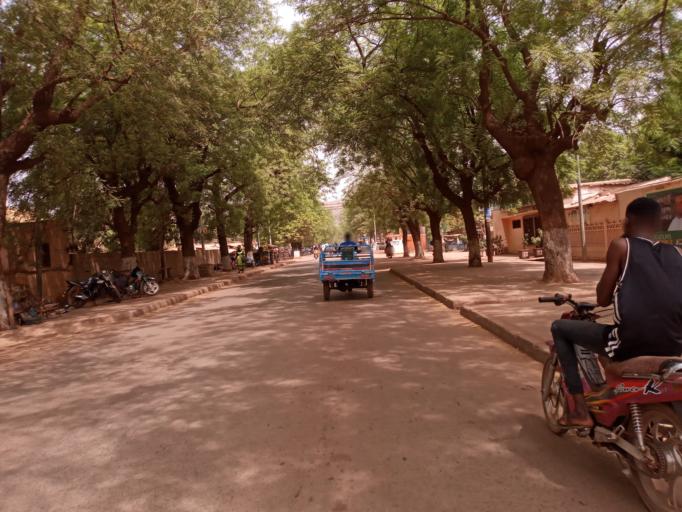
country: ML
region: Bamako
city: Bamako
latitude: 12.6515
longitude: -7.9812
